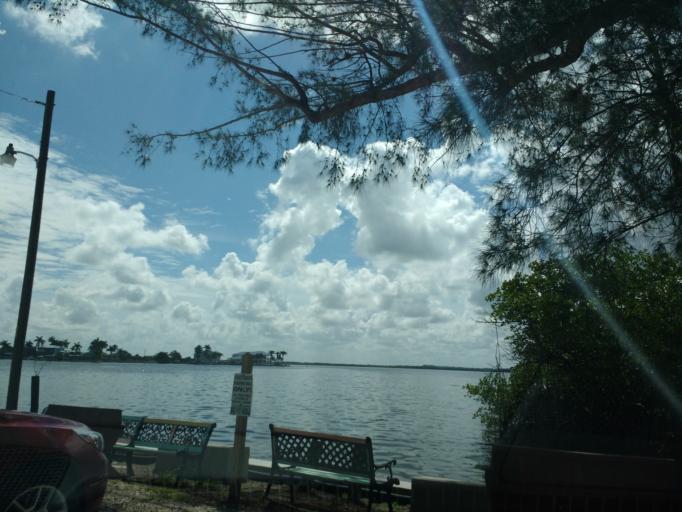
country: US
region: Florida
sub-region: Lee County
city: Pine Island Center
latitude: 26.6242
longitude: -82.0751
